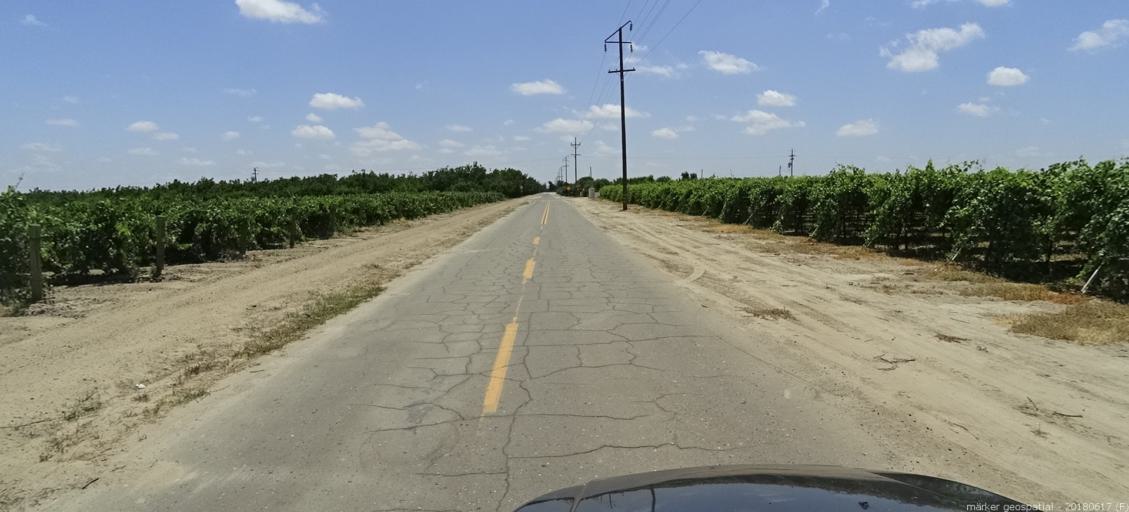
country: US
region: California
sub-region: Fresno County
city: Biola
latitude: 36.8235
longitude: -120.1150
